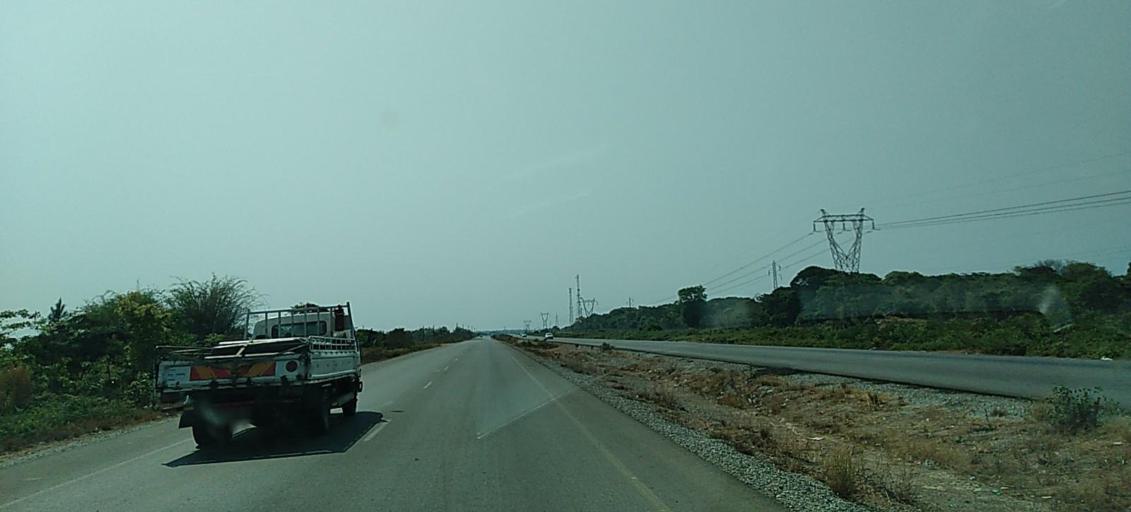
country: ZM
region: Copperbelt
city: Chingola
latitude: -12.5905
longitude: 27.9475
